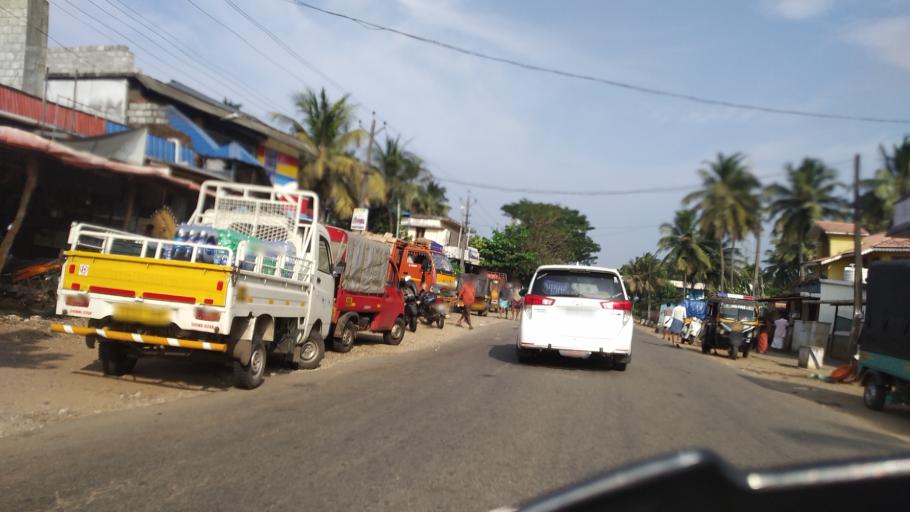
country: IN
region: Kerala
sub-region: Thrissur District
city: Chelakara
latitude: 10.5885
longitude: 76.5128
